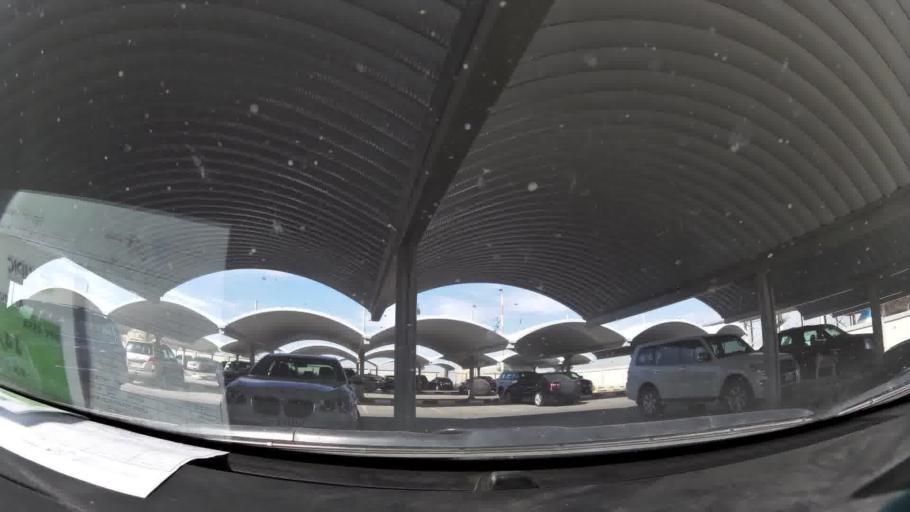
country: KW
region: Al Farwaniyah
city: Janub as Surrah
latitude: 29.2278
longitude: 47.9840
